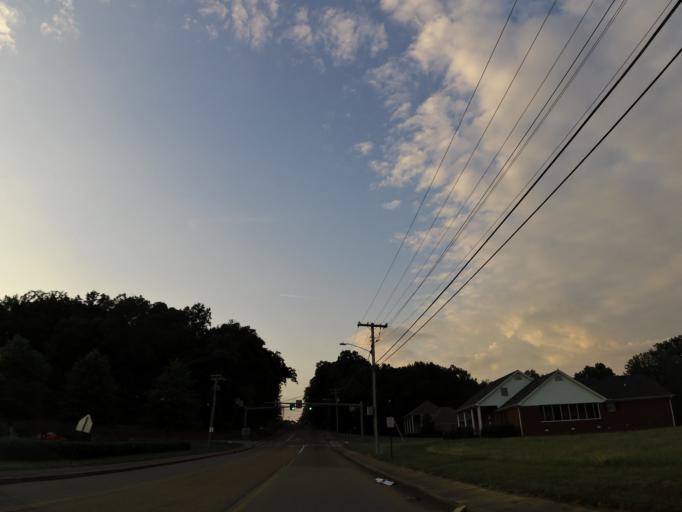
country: US
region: Tennessee
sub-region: Henry County
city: Paris
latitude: 36.2929
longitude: -88.3029
